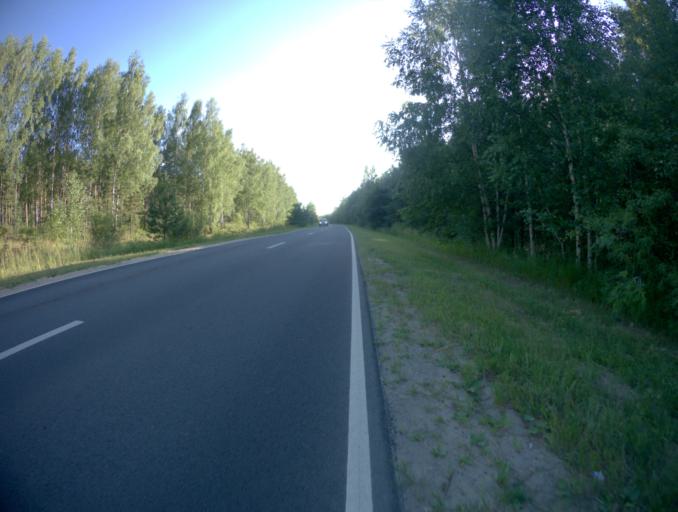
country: RU
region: Nizjnij Novgorod
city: Taremskoye
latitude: 56.0133
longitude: 42.9366
